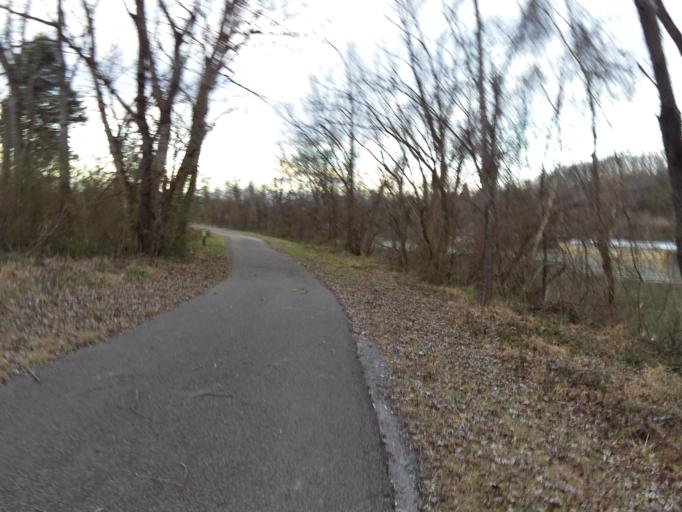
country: US
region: Tennessee
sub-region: Knox County
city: Knoxville
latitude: 35.9573
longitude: -83.8453
